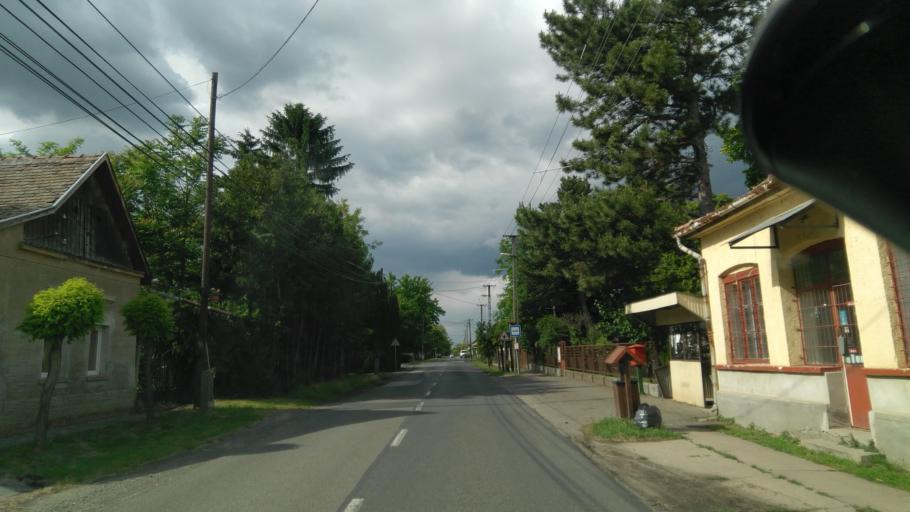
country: HU
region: Bekes
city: Gadoros
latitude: 46.6634
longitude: 20.5901
